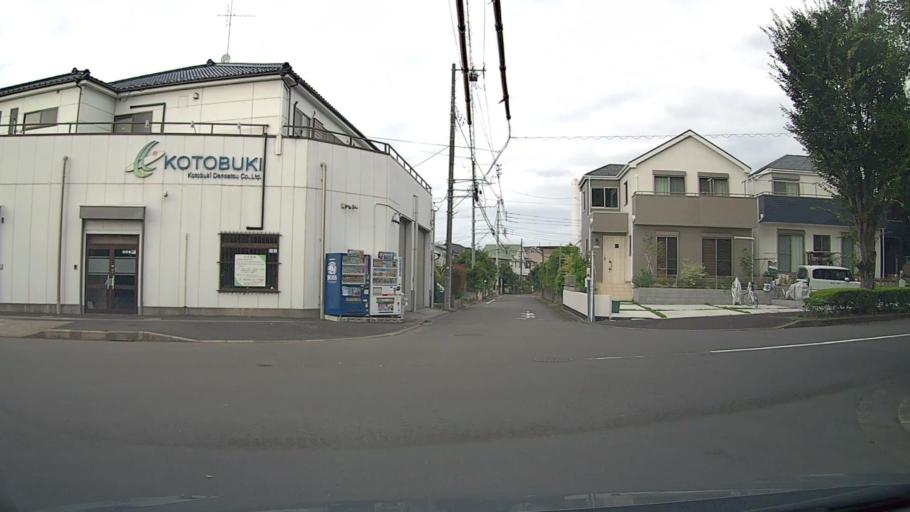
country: JP
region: Tokyo
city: Higashimurayama-shi
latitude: 35.7525
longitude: 139.4897
